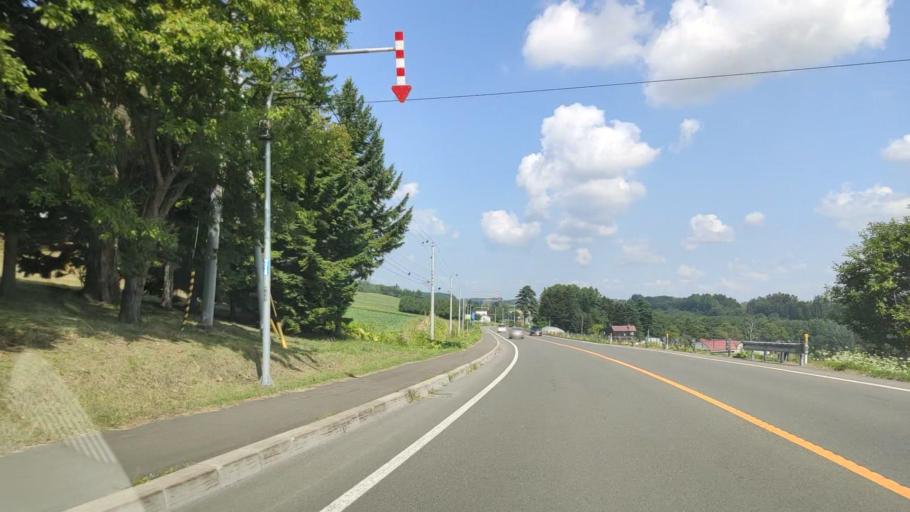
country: JP
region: Hokkaido
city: Shimo-furano
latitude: 43.5221
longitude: 142.4477
